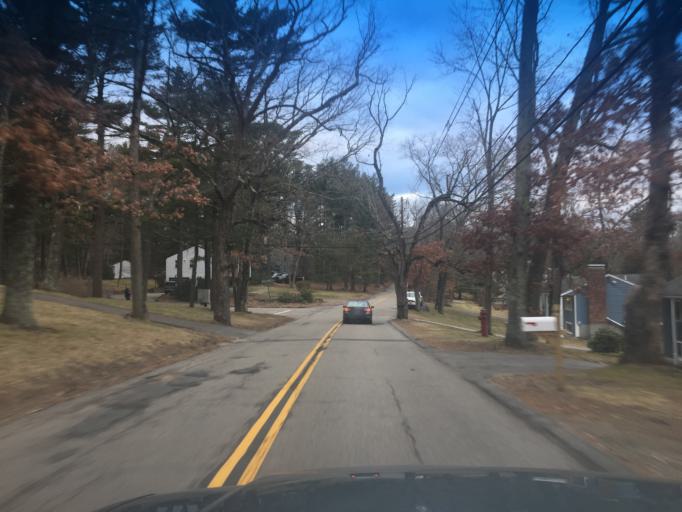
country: US
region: Massachusetts
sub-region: Norfolk County
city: Medway
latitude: 42.1470
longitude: -71.3813
